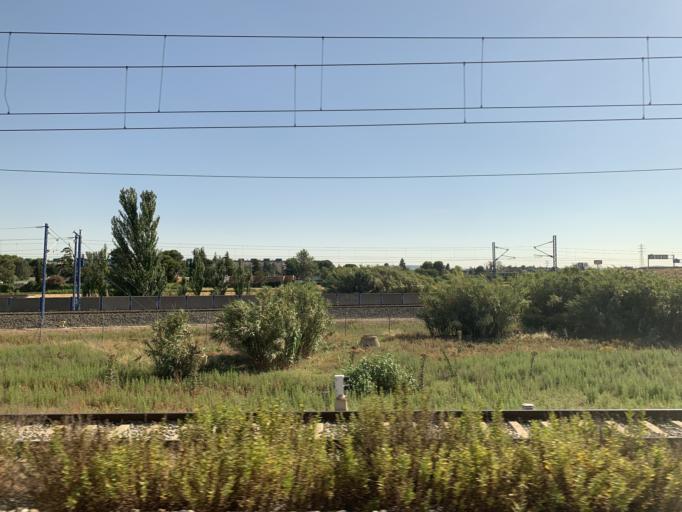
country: ES
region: Aragon
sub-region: Provincia de Zaragoza
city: Oliver-Valdefierro, Oliver, Valdefierro
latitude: 41.6695
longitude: -0.9305
